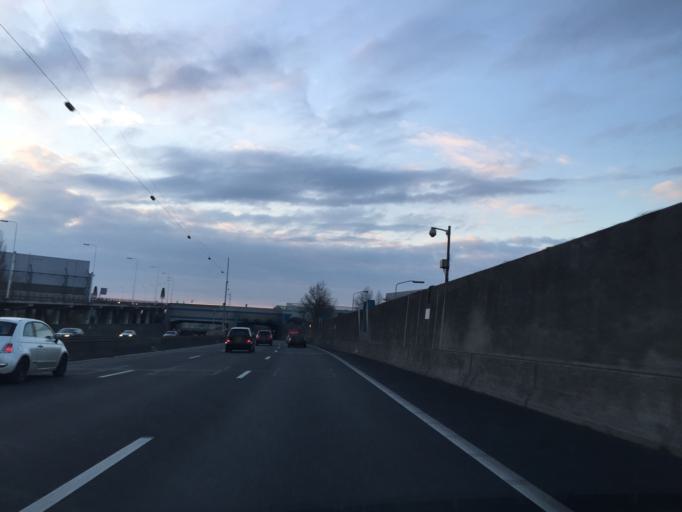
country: NL
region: South Holland
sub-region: Gemeente Alblasserdam
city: Alblasserdam
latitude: 51.8575
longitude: 4.6632
